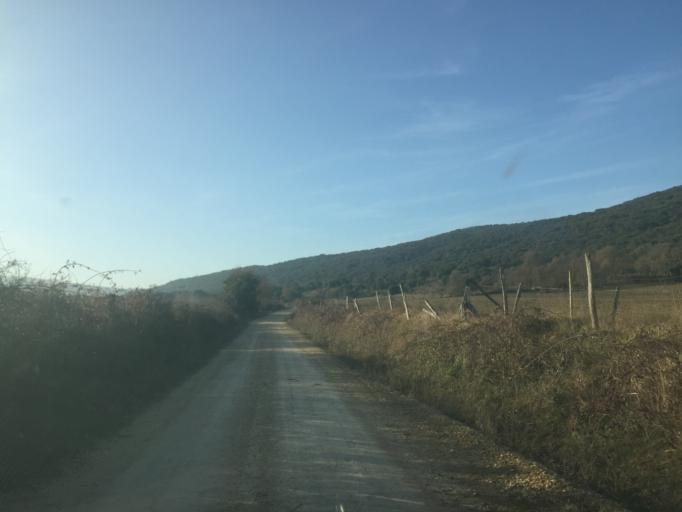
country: ES
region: Castille and Leon
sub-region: Provincia de Burgos
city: Medina de Pomar
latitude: 42.9289
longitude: -3.5936
